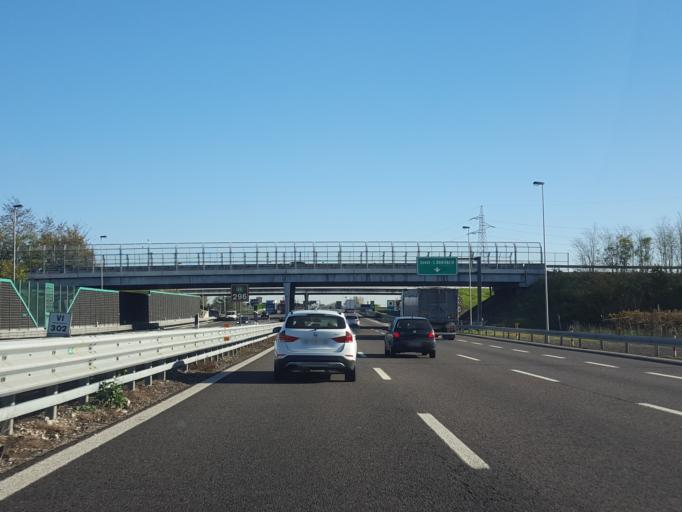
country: IT
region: Veneto
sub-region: Provincia di Verona
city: Soave
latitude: 45.4098
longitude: 11.2460
